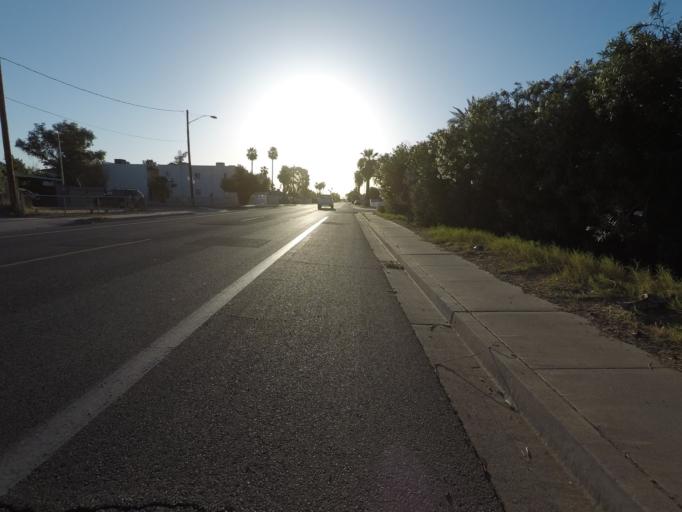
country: US
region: Arizona
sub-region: Maricopa County
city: Phoenix
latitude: 33.4730
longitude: -112.0221
